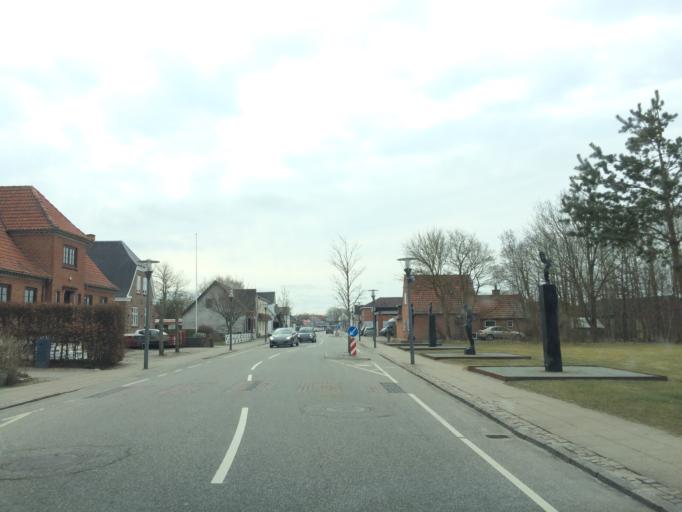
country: DK
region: Central Jutland
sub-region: Ringkobing-Skjern Kommune
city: Tarm
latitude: 55.9115
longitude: 8.5204
